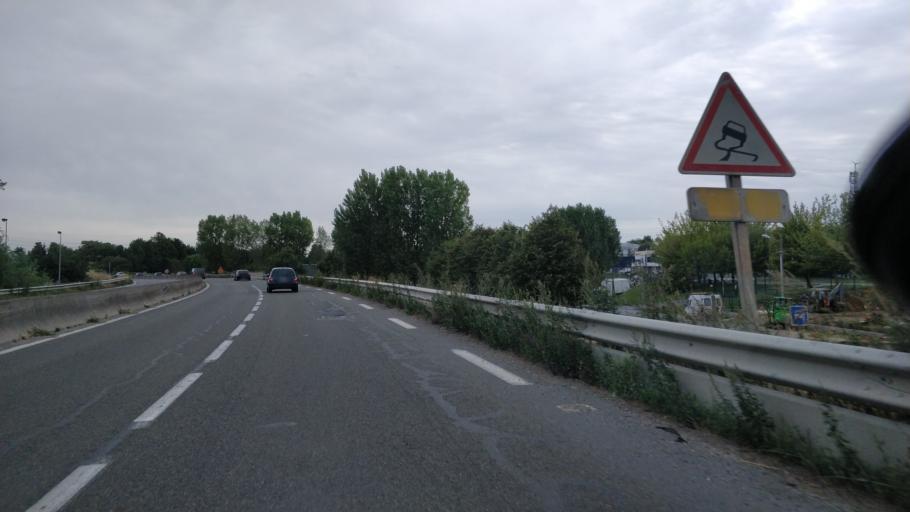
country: FR
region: Ile-de-France
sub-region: Departement de Seine-et-Marne
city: Villeparisis
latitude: 48.9359
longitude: 2.6190
